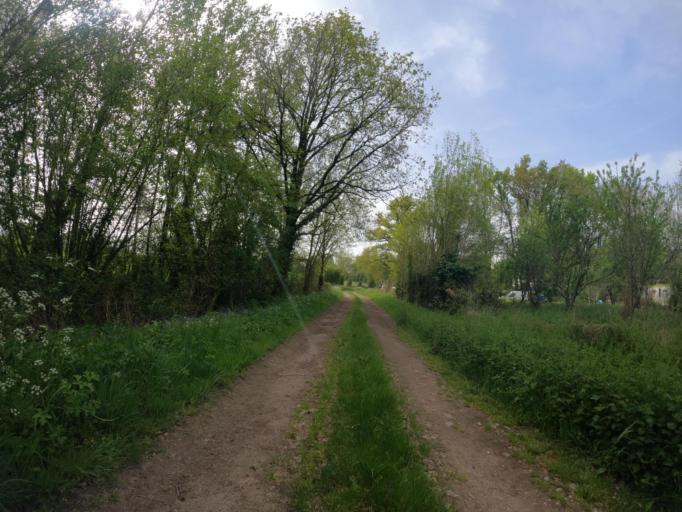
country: FR
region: Poitou-Charentes
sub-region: Departement des Deux-Sevres
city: La Chapelle-Saint-Laurent
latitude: 46.6973
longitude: -0.5085
